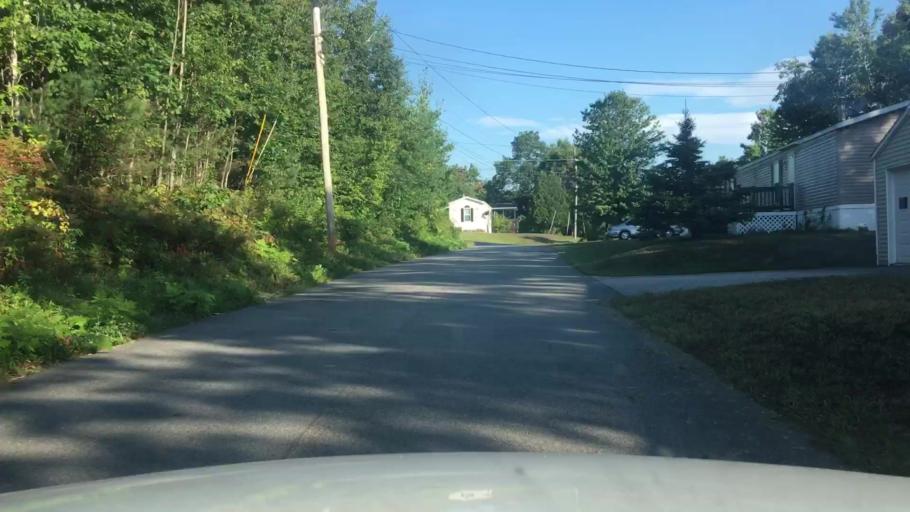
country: US
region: Maine
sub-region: Oxford County
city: Norway
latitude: 44.1983
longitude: -70.5366
